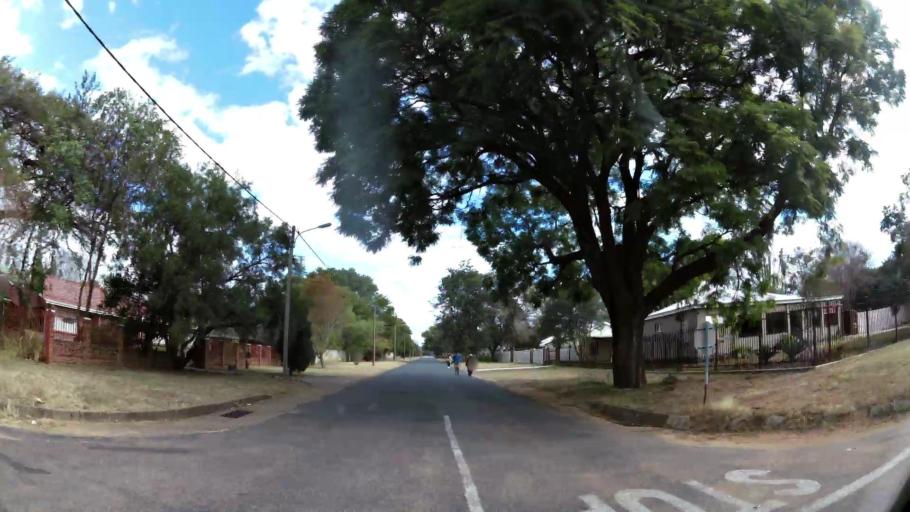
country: ZA
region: Limpopo
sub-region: Waterberg District Municipality
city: Modimolle
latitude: -24.7085
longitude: 28.4064
